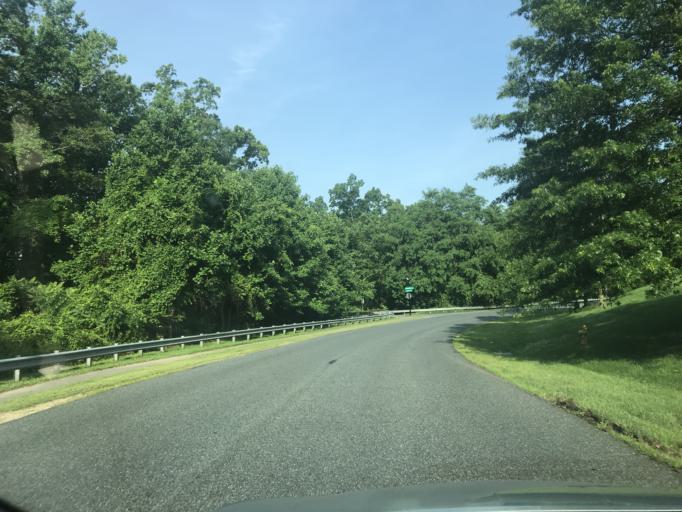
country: US
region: Maryland
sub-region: Harford County
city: Bel Air North
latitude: 39.5536
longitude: -76.3588
